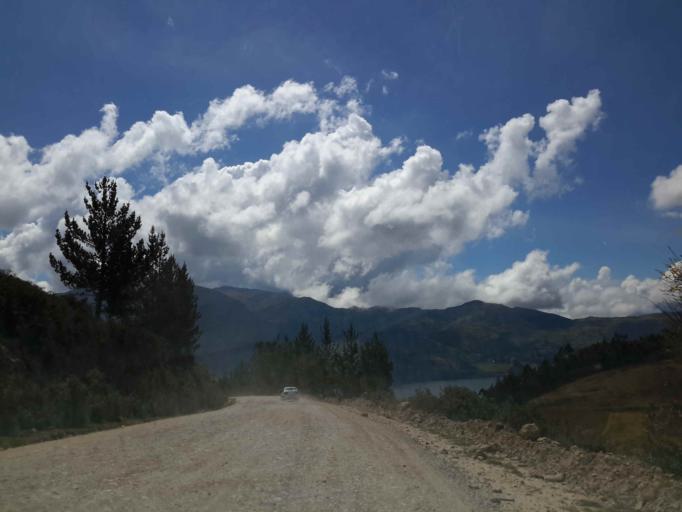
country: PE
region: Apurimac
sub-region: Provincia de Andahuaylas
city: Pacucha
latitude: -13.6282
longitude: -73.3384
